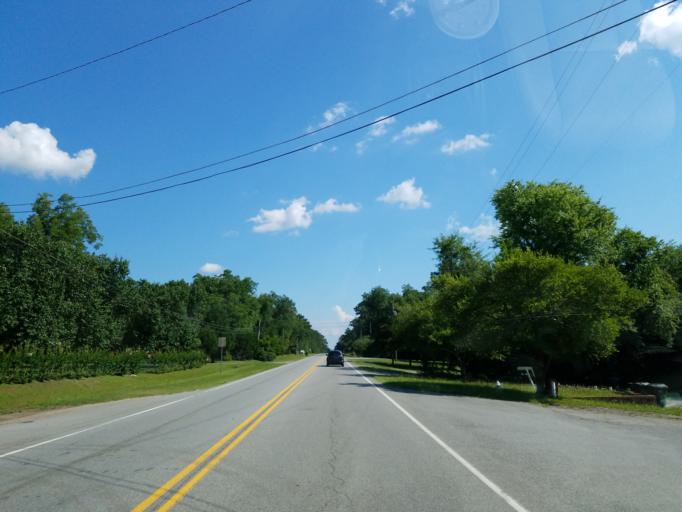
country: US
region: Georgia
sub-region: Crawford County
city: Roberta
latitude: 32.7159
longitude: -84.0108
